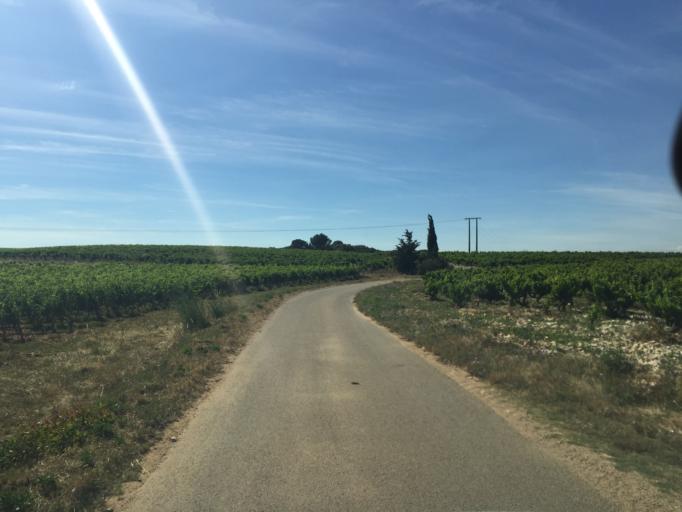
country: FR
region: Provence-Alpes-Cote d'Azur
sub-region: Departement du Vaucluse
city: Chateauneuf-du-Pape
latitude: 44.0686
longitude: 4.8073
